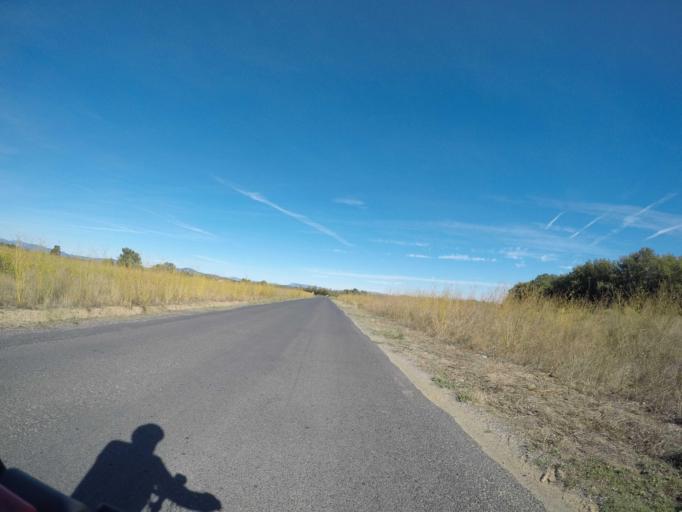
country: FR
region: Languedoc-Roussillon
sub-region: Departement des Pyrenees-Orientales
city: Ponteilla
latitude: 42.6443
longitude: 2.8024
